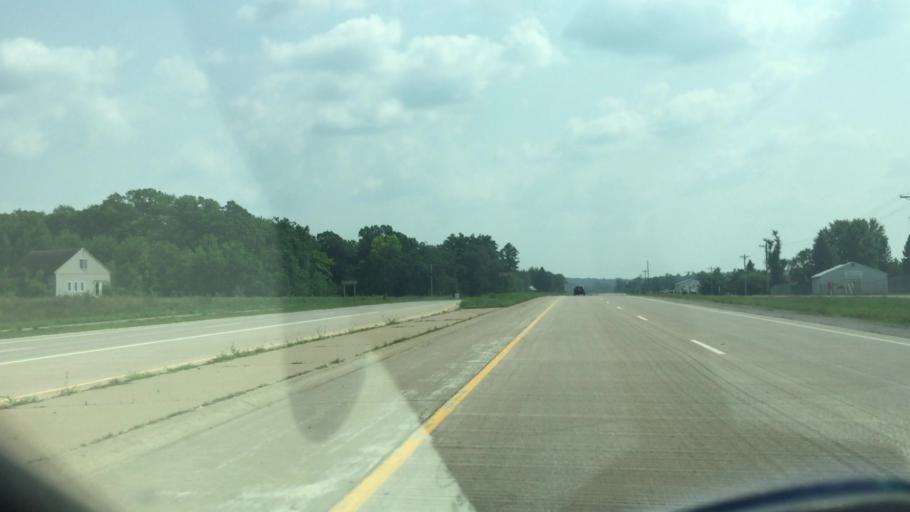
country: US
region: Wisconsin
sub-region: Eau Claire County
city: Altoona
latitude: 44.7514
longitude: -91.4537
